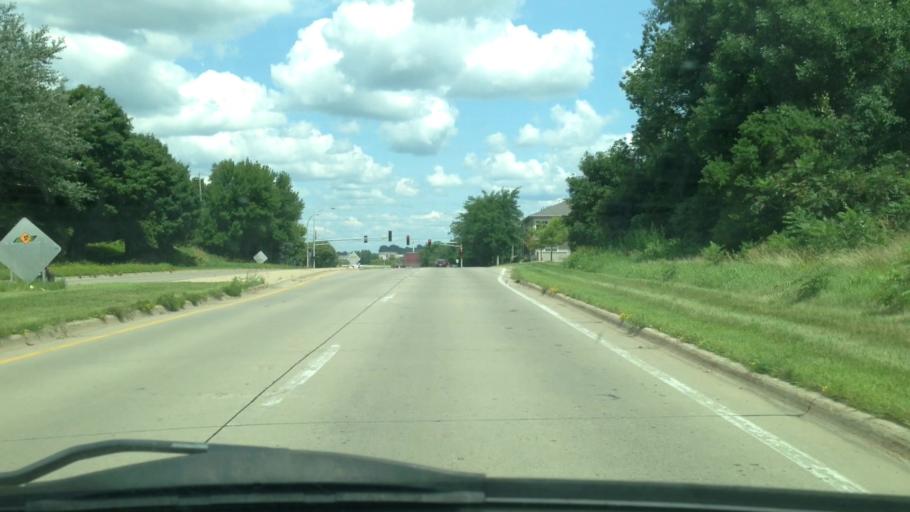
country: US
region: Minnesota
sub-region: Olmsted County
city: Rochester
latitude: 44.0308
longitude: -92.5163
